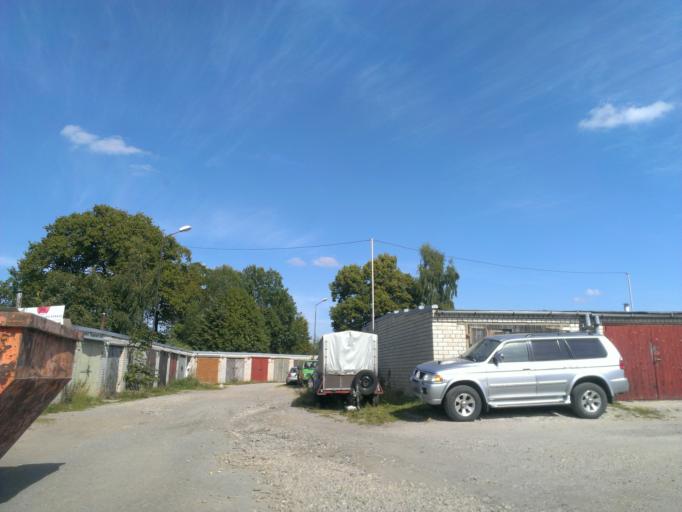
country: LV
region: Adazi
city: Adazi
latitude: 57.0830
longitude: 24.3194
